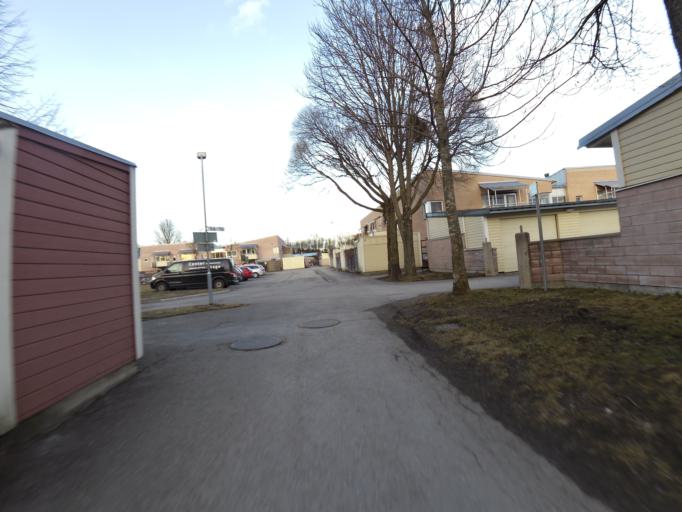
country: SE
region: Gaevleborg
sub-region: Gavle Kommun
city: Gavle
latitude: 60.6596
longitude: 17.1679
